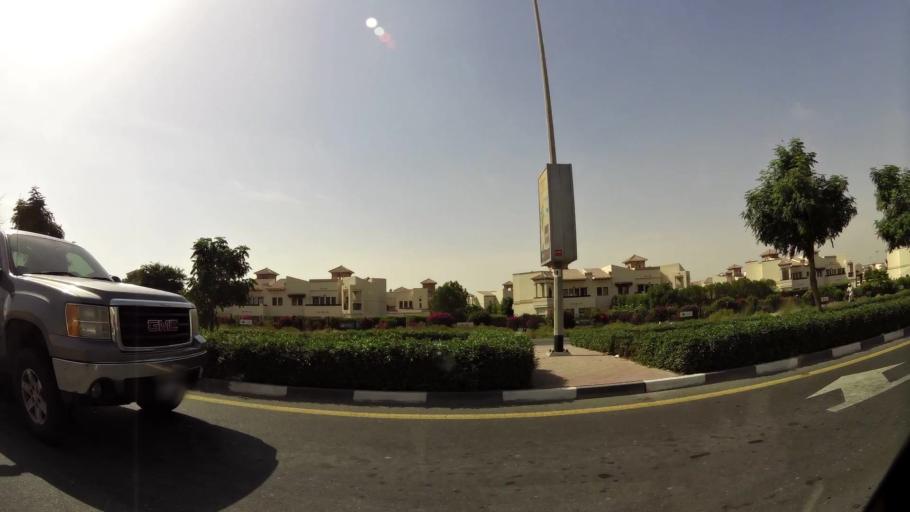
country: AE
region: Ash Shariqah
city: Sharjah
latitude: 25.2138
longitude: 55.4255
